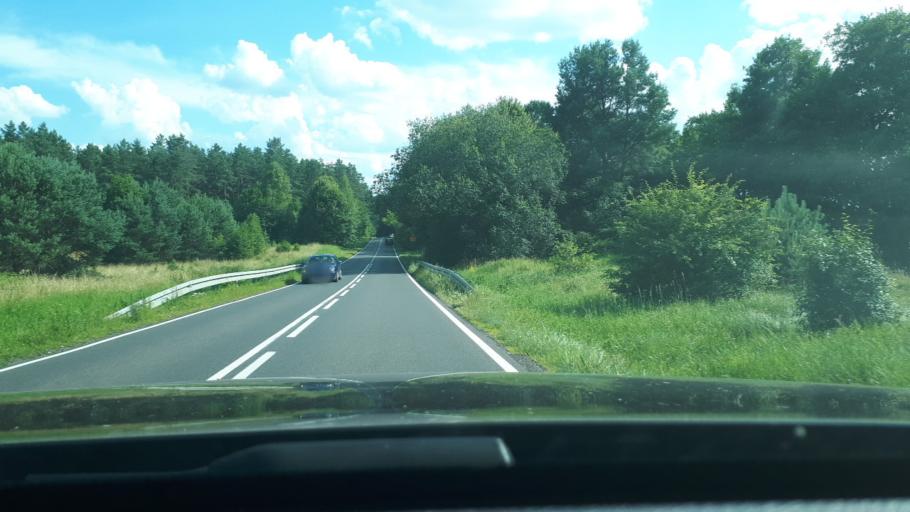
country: PL
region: Warmian-Masurian Voivodeship
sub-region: Powiat olsztynski
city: Stawiguda
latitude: 53.5448
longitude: 20.4197
